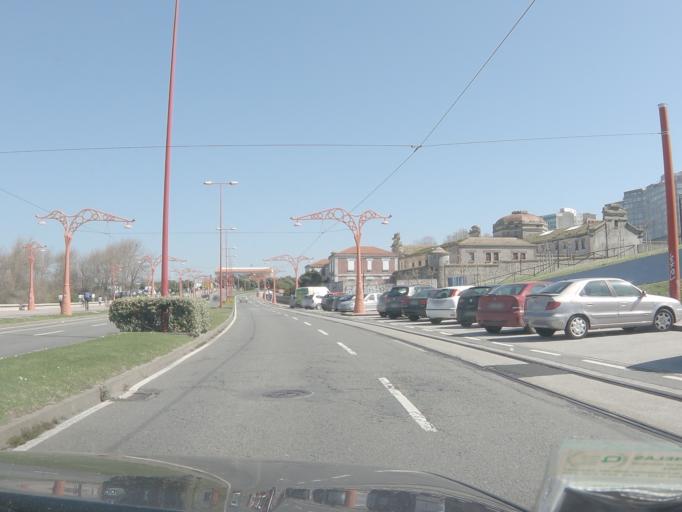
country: ES
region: Galicia
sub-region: Provincia da Coruna
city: A Coruna
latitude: 43.3826
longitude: -8.4061
